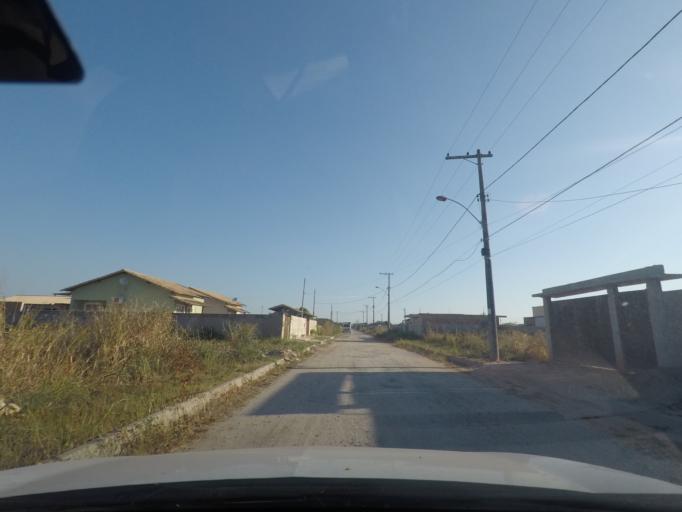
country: BR
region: Rio de Janeiro
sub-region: Marica
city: Marica
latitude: -22.9604
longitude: -42.9361
